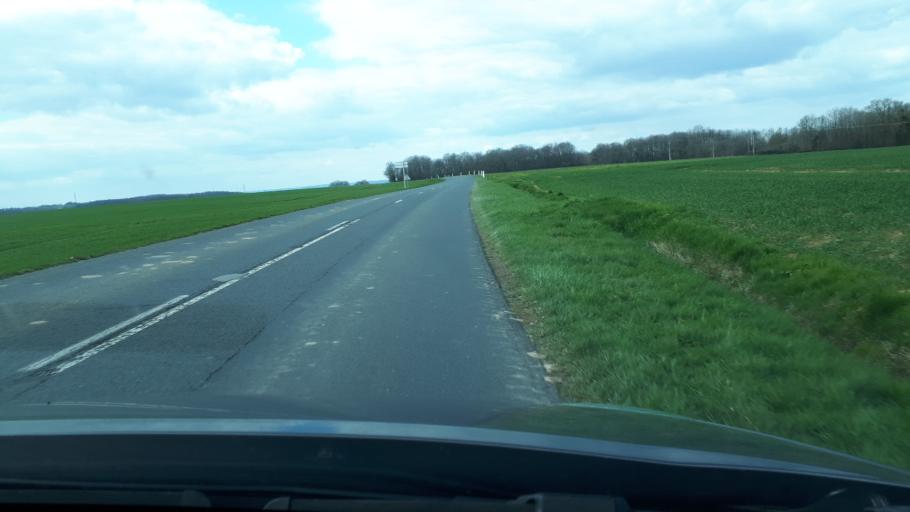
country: FR
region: Centre
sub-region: Departement du Loir-et-Cher
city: Lunay
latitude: 47.7619
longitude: 0.9461
